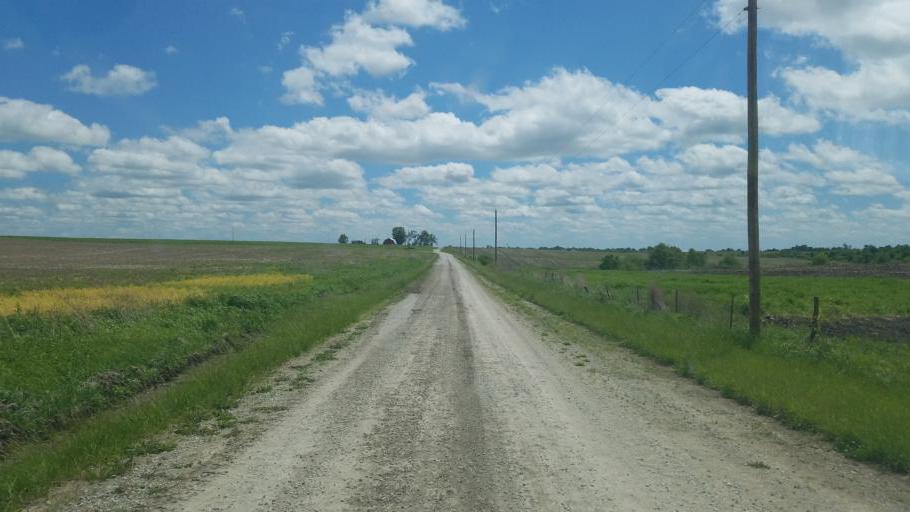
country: US
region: Iowa
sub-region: Decatur County
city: Lamoni
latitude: 40.4998
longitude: -93.9839
